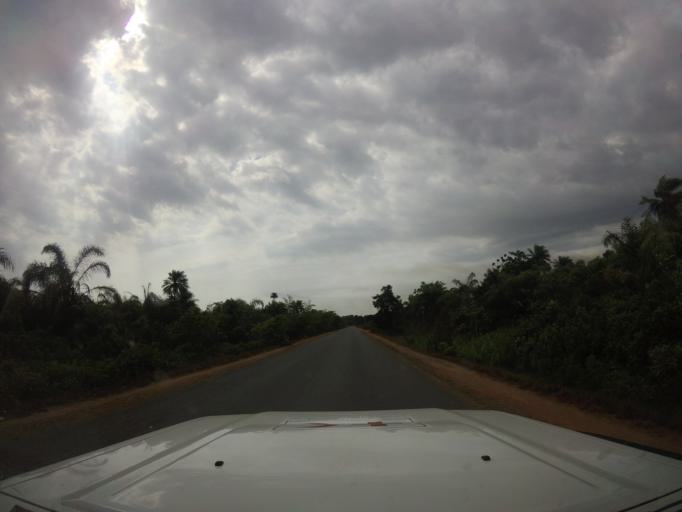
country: LR
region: Montserrado
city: Monrovia
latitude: 6.5336
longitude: -10.8510
